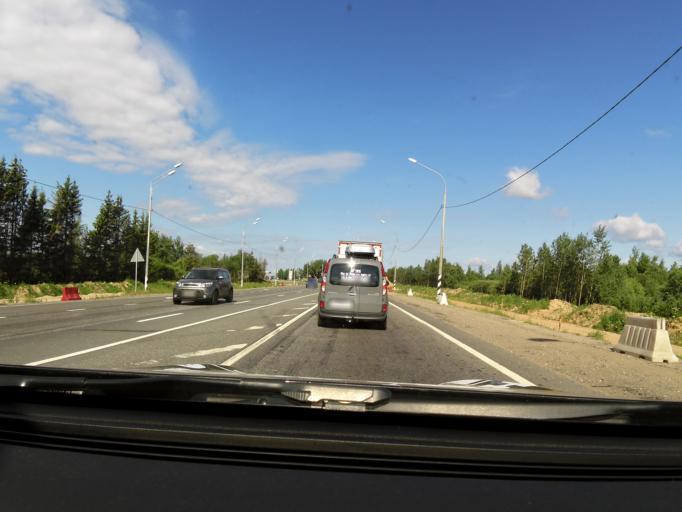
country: RU
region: Tverskaya
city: Tver
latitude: 56.7848
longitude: 35.9340
